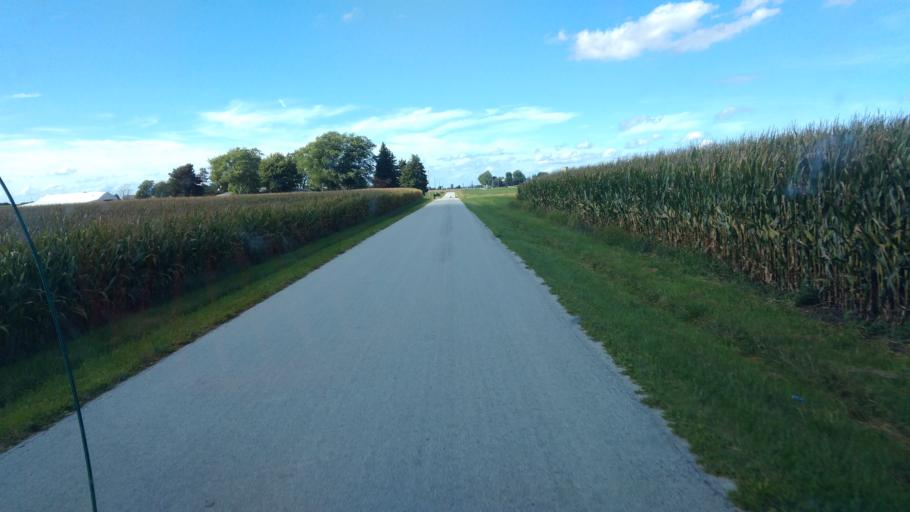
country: US
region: Ohio
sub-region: Hardin County
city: Kenton
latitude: 40.7270
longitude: -83.6723
